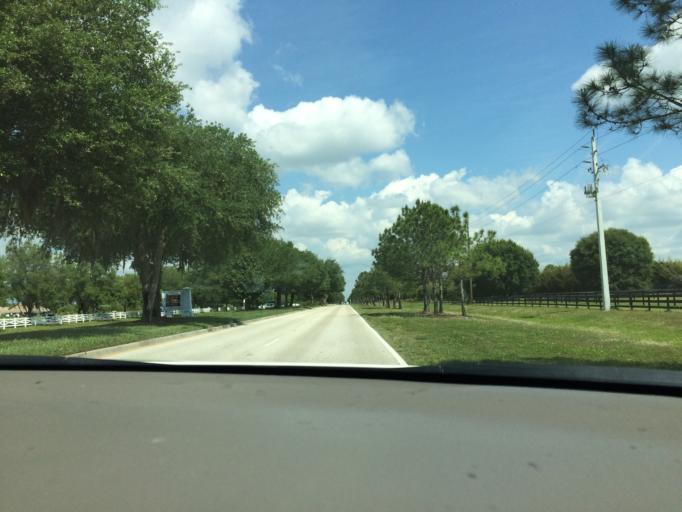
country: US
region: Florida
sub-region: Sarasota County
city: The Meadows
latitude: 27.3864
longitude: -82.4144
